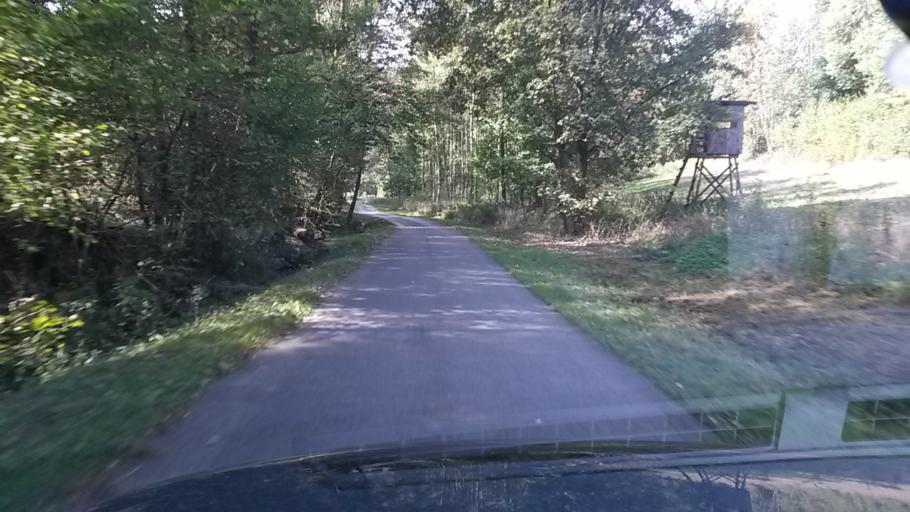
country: DE
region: North Rhine-Westphalia
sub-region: Regierungsbezirk Arnsberg
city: Herscheid
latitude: 51.1905
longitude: 7.7165
